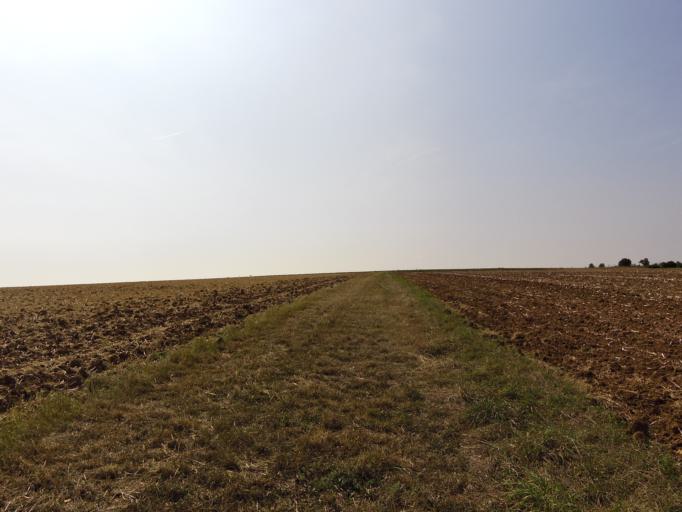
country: DE
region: Bavaria
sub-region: Regierungsbezirk Unterfranken
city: Estenfeld
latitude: 49.8315
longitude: 10.0153
